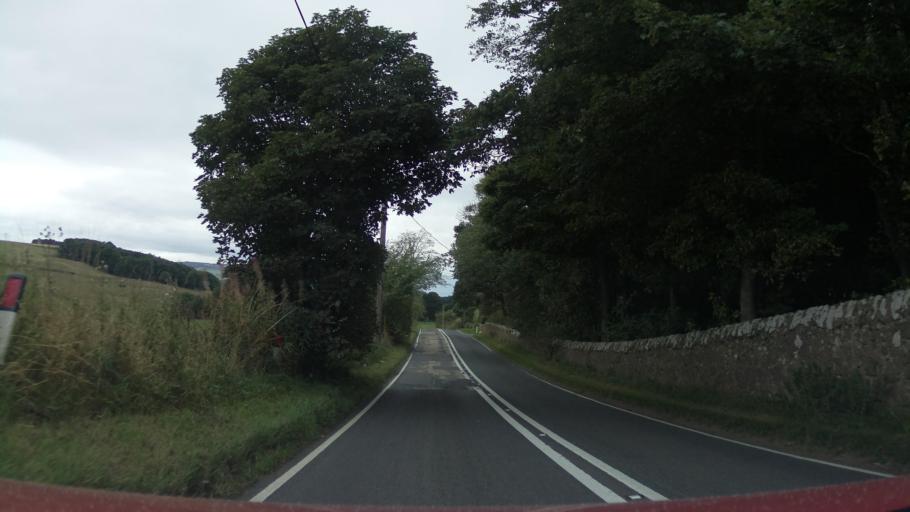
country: GB
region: Scotland
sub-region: Fife
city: Kinglassie
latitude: 56.1997
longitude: -3.2461
